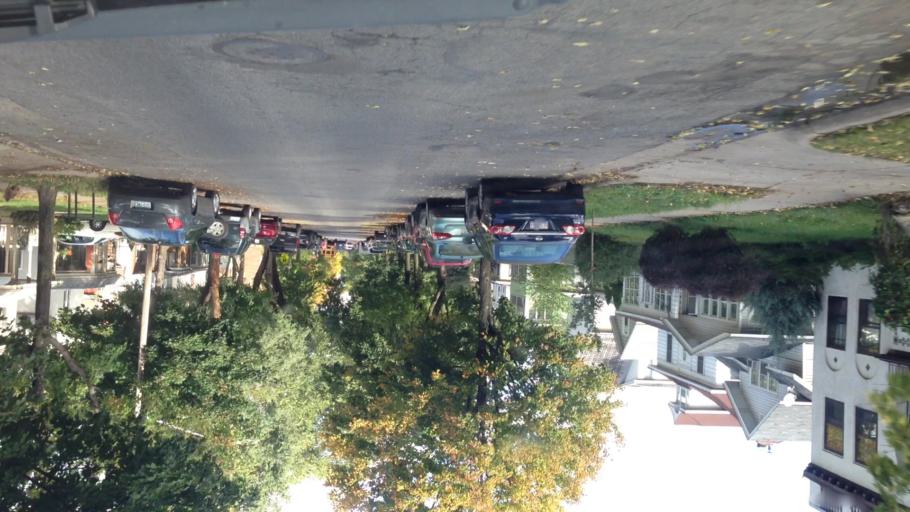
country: US
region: Minnesota
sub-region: Hennepin County
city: Minneapolis
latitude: 44.9523
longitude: -93.2855
